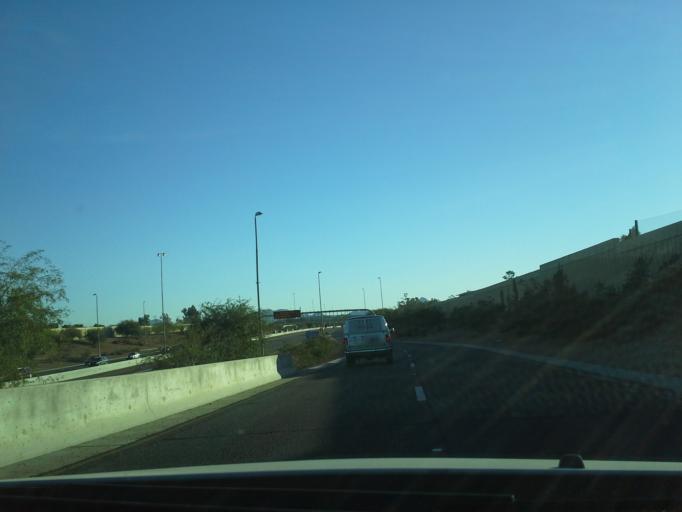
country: US
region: Arizona
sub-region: Maricopa County
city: Paradise Valley
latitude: 33.6539
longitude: -112.0007
